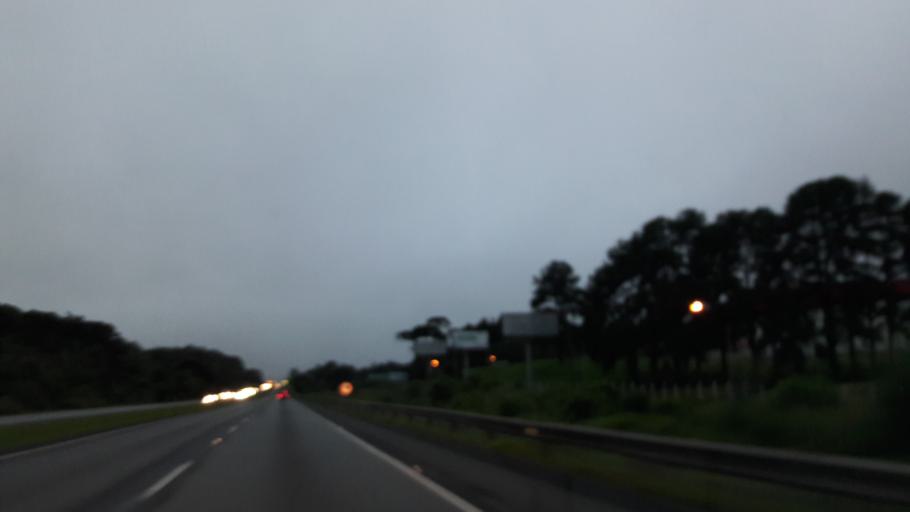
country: BR
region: Parana
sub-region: Piraquara
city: Piraquara
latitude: -25.5336
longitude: -49.0778
